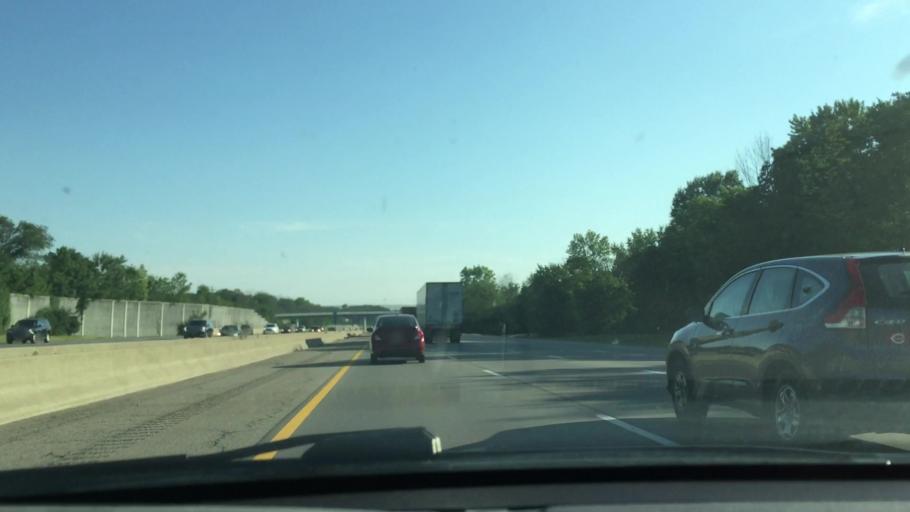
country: US
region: Ohio
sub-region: Warren County
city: Landen
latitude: 39.3138
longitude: -84.2940
